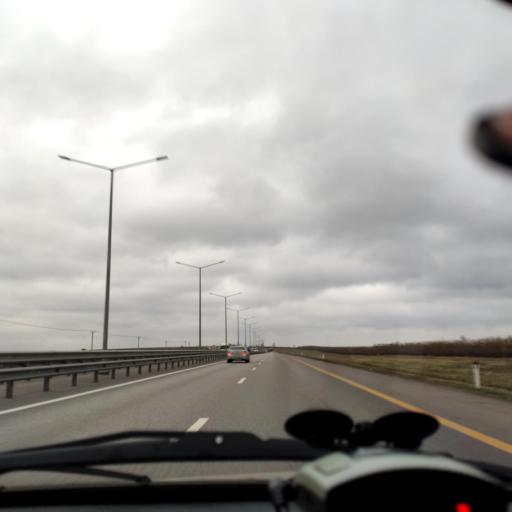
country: RU
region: Voronezj
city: Novaya Usman'
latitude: 51.5962
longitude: 39.3565
